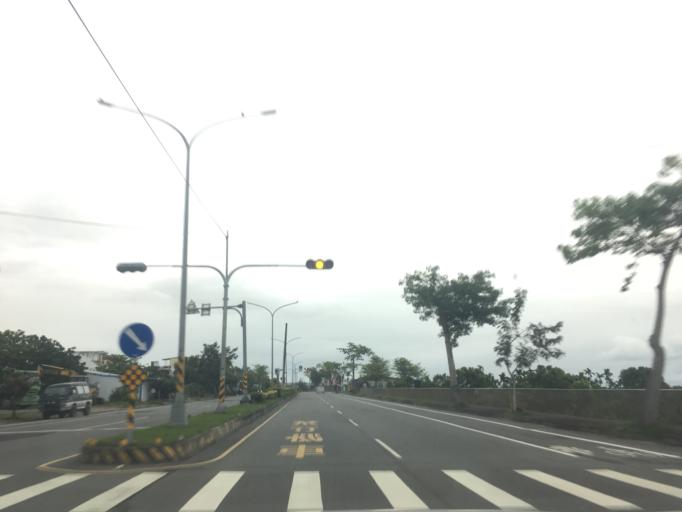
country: TW
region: Taiwan
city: Taitung City
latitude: 22.7160
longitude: 121.0492
